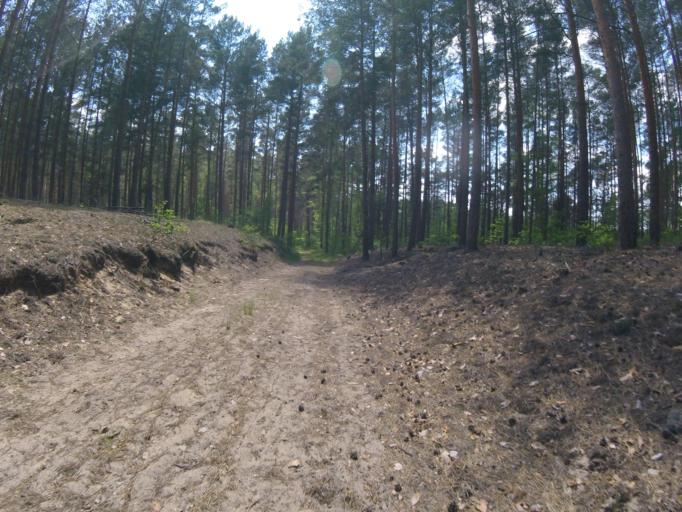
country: DE
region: Brandenburg
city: Teupitz
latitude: 52.1077
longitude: 13.5975
